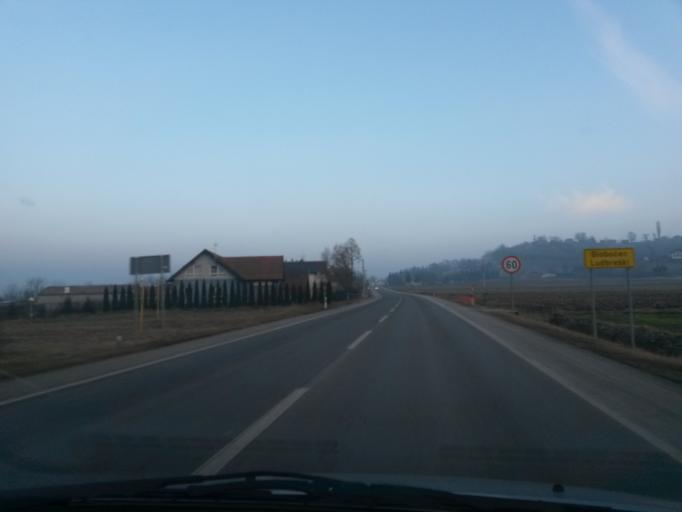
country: HR
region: Varazdinska
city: Ludbreg
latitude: 46.2400
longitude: 16.6331
